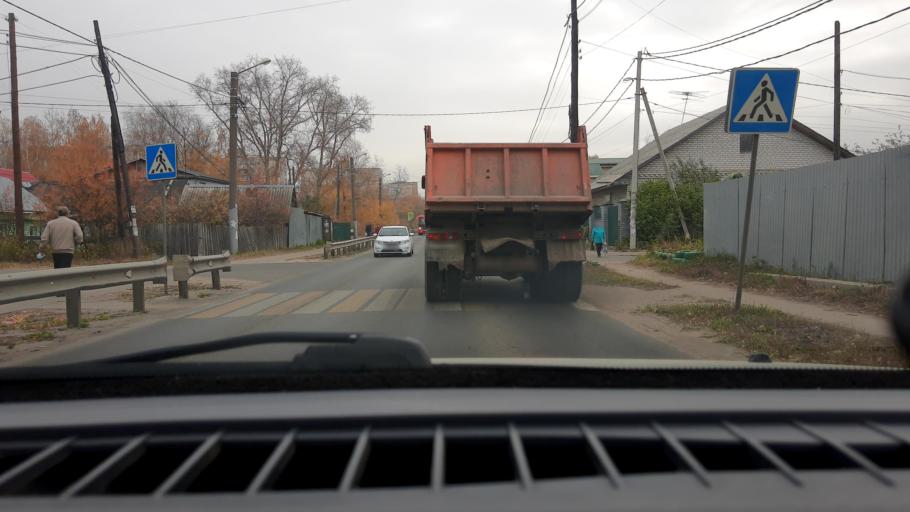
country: RU
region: Nizjnij Novgorod
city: Gorbatovka
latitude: 56.3313
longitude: 43.8315
